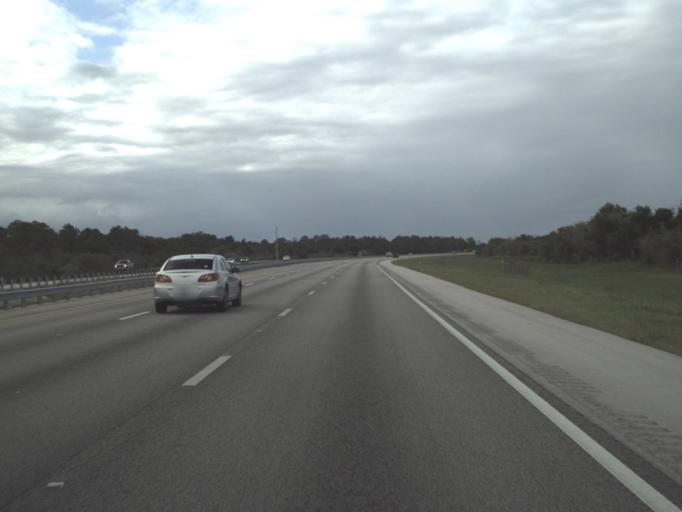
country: US
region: Florida
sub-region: Lee County
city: Suncoast Estates
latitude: 26.7561
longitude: -81.8690
